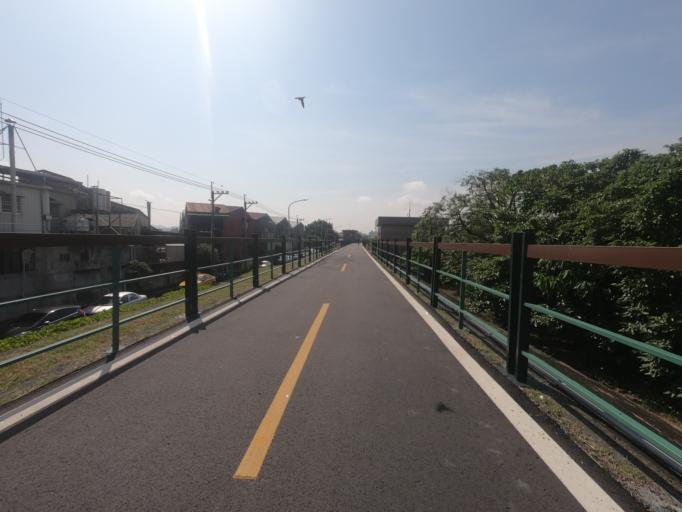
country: TW
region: Taipei
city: Taipei
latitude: 25.0994
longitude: 121.4898
